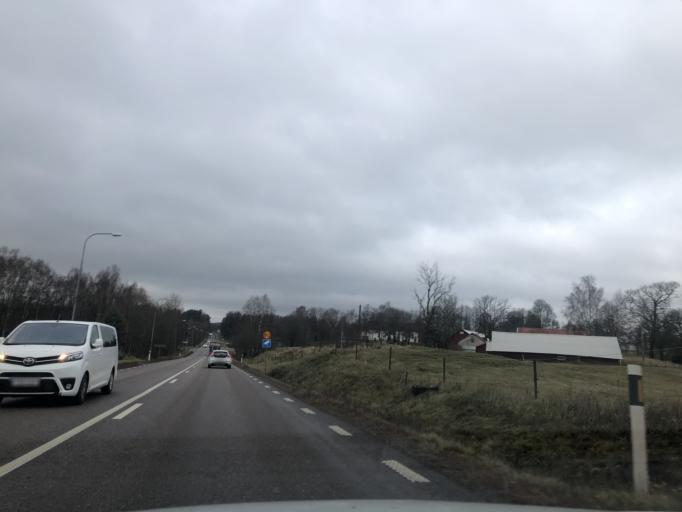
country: SE
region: Vaestra Goetaland
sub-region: Ulricehamns Kommun
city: Ulricehamn
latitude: 57.8497
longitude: 13.4373
